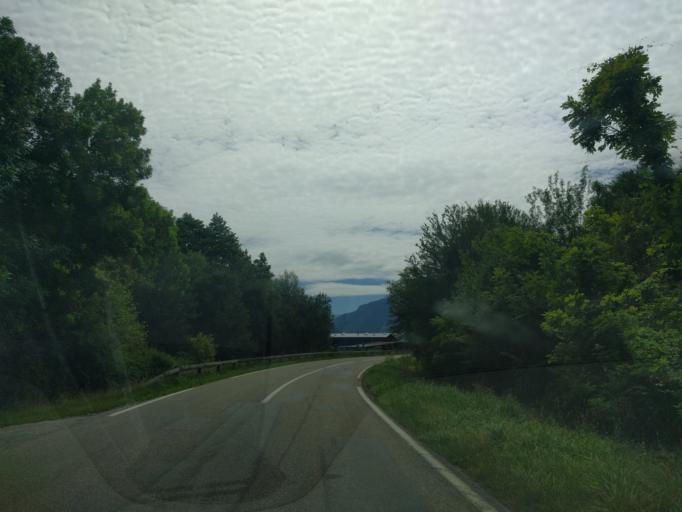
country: FR
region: Rhone-Alpes
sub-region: Departement de la Savoie
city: Saint-Remy-de-Maurienne
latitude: 45.3852
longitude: 6.2724
